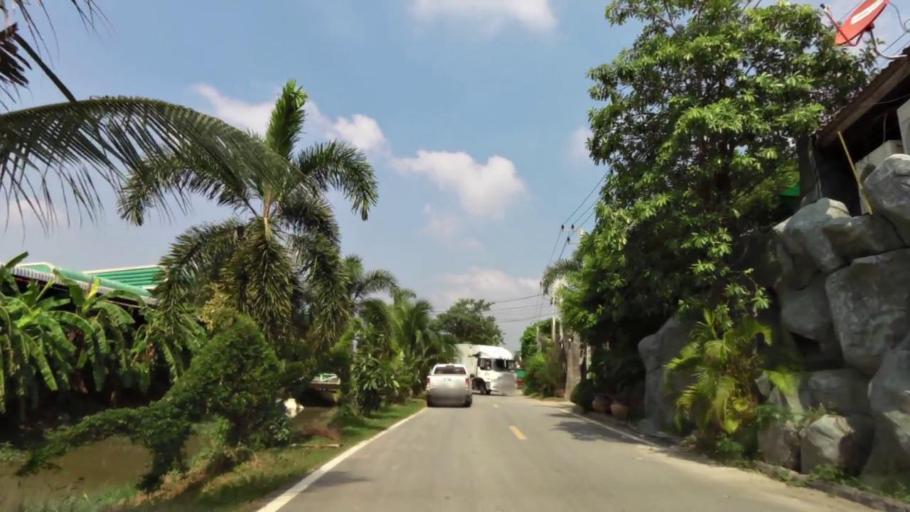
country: TH
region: Ang Thong
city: Ang Thong
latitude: 14.6091
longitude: 100.3979
